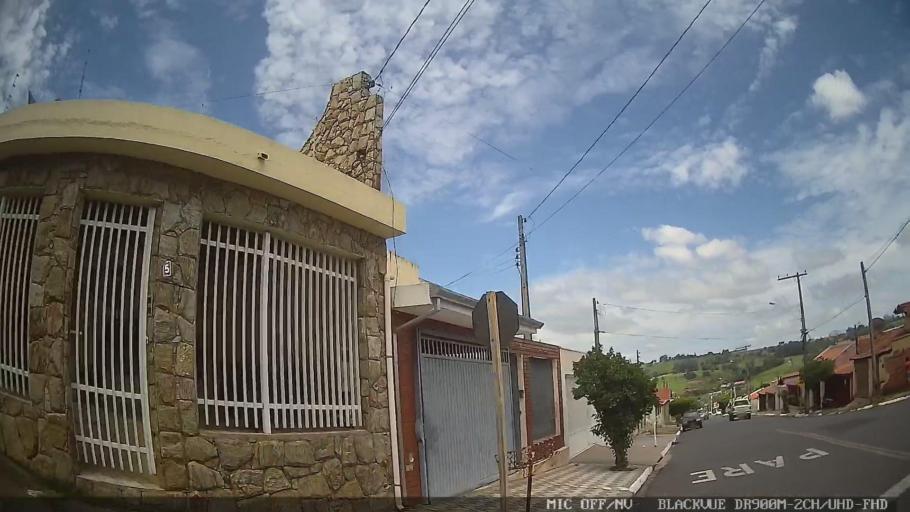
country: BR
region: Sao Paulo
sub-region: Laranjal Paulista
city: Laranjal Paulista
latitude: -23.0375
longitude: -47.8314
